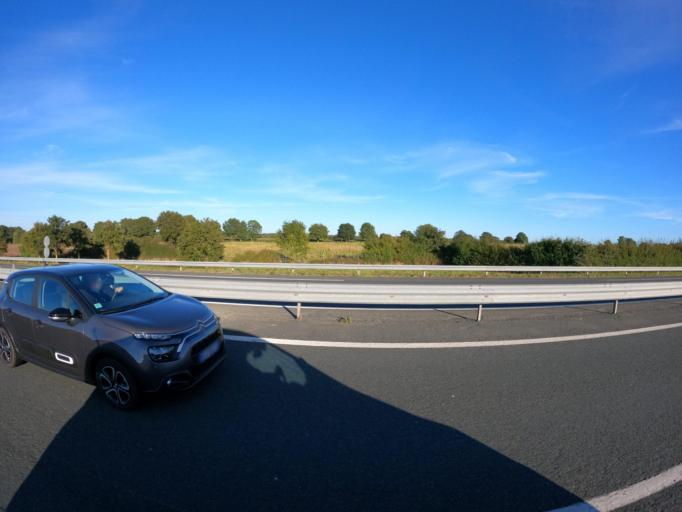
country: FR
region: Pays de la Loire
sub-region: Departement de Maine-et-Loire
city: Mazieres-en-Mauges
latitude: 47.0707
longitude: -0.8263
